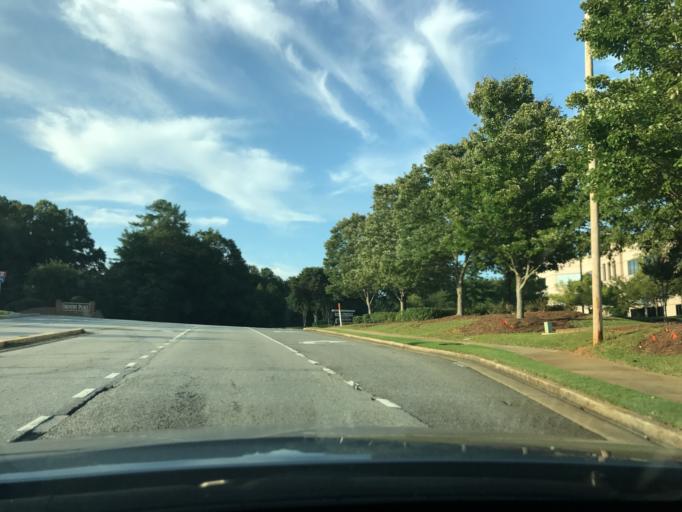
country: US
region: Georgia
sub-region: Fulton County
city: Alpharetta
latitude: 34.0696
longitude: -84.2677
